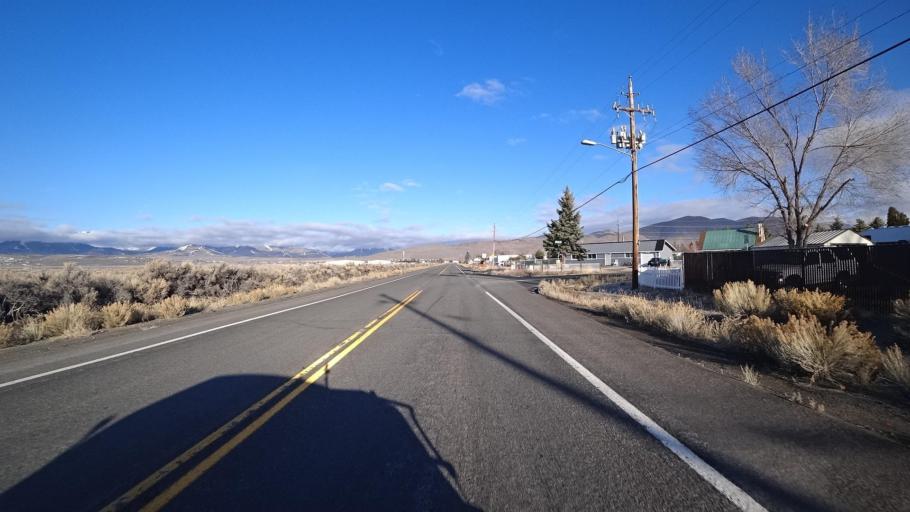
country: US
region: Nevada
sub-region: Washoe County
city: Cold Springs
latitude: 39.6710
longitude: -119.9650
